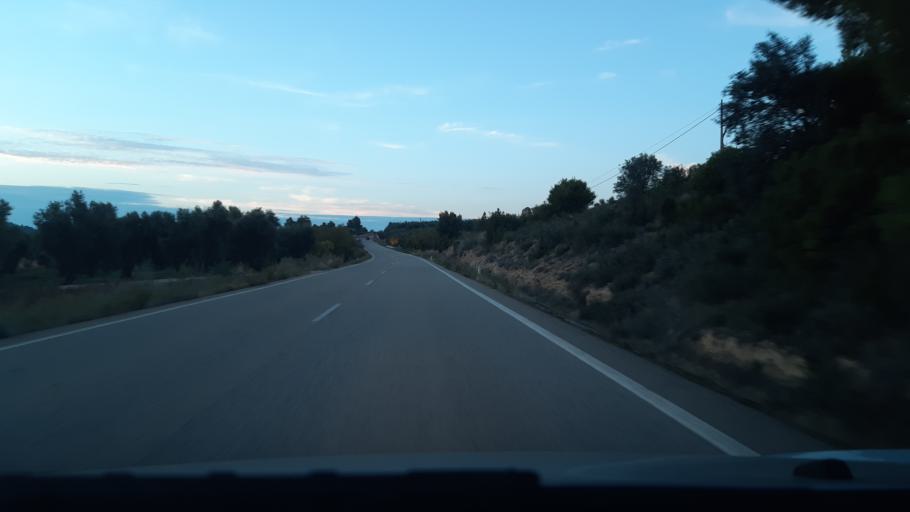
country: ES
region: Aragon
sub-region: Provincia de Teruel
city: Valderrobres
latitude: 40.8562
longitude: 0.1716
